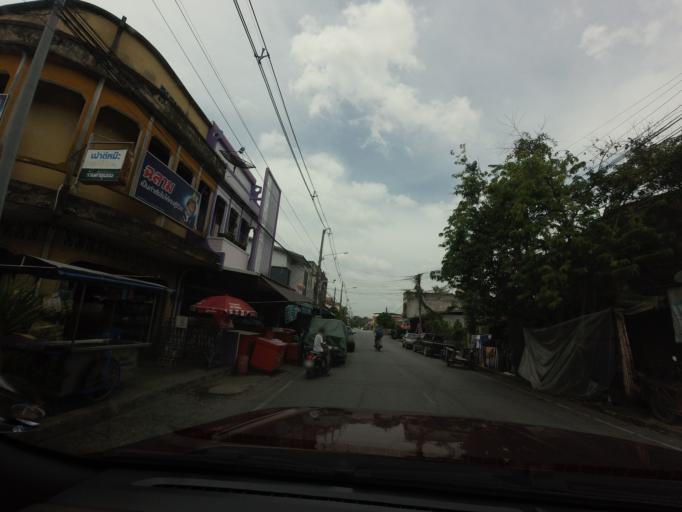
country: TH
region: Yala
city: Yala
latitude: 6.5621
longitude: 101.2963
